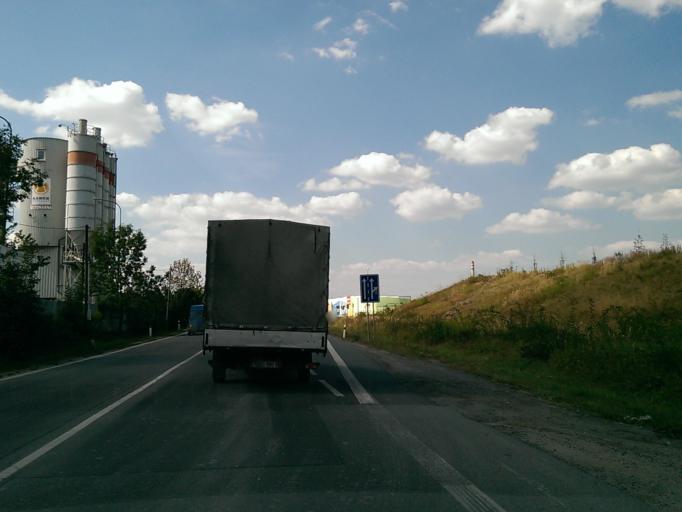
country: CZ
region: Praha
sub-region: Praha 14
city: Hostavice
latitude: 50.0647
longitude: 14.5511
